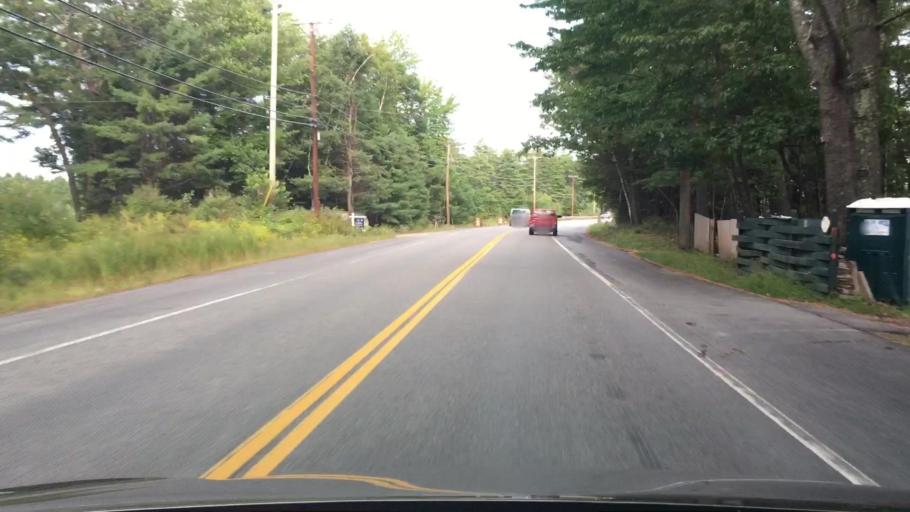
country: US
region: Maine
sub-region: Oxford County
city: Denmark
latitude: 44.0655
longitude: -70.8134
